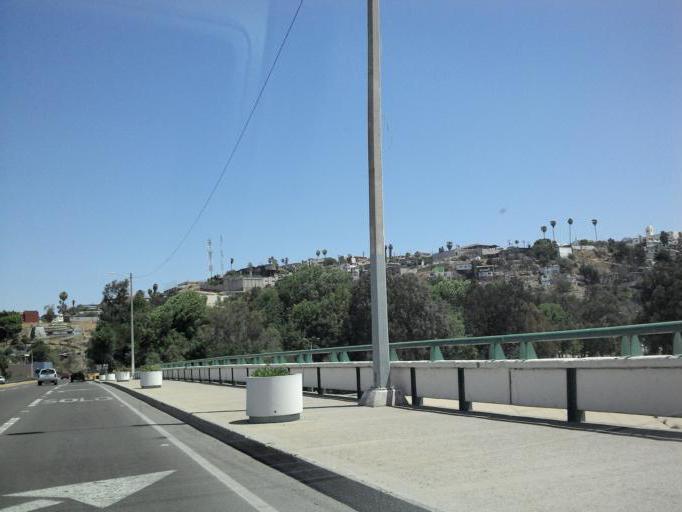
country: MX
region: Baja California
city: Tijuana
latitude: 32.5227
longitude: -117.0082
